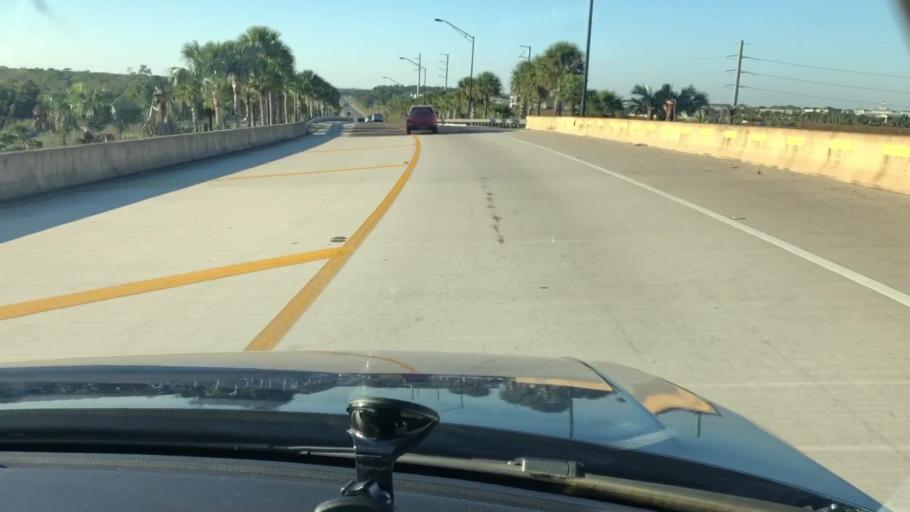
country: US
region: Florida
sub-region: Polk County
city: Loughman
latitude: 28.2834
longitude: -81.5933
